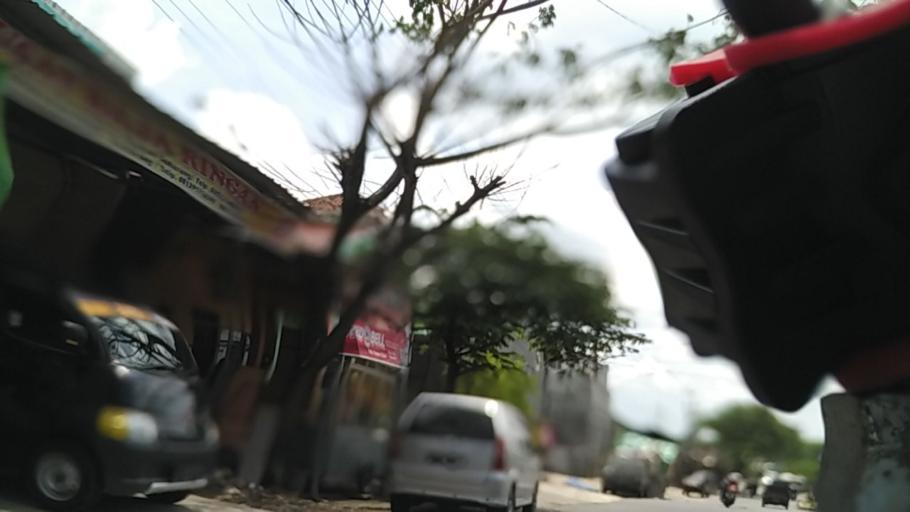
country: ID
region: Central Java
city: Semarang
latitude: -7.0182
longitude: 110.3381
